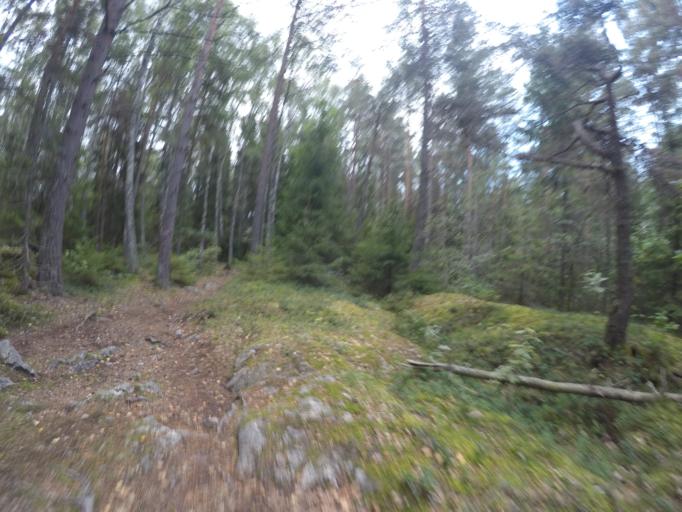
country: SE
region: Vaestmanland
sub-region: Vasteras
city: Vasteras
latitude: 59.6441
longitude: 16.5213
